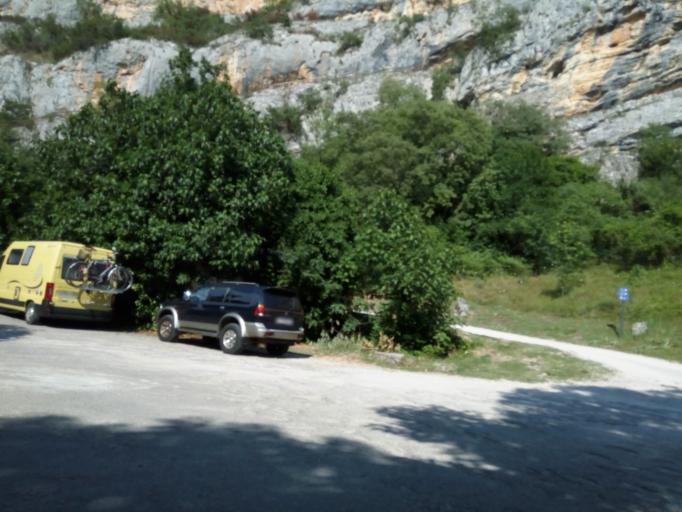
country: HR
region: Sibensko-Kniniska
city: Kistanje
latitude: 43.9044
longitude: 15.9776
